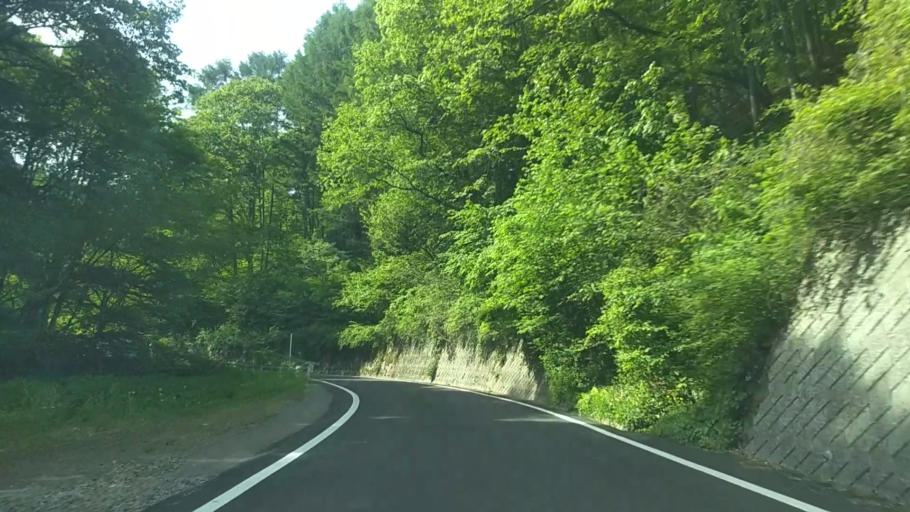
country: JP
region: Nagano
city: Saku
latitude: 36.1125
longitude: 138.4708
